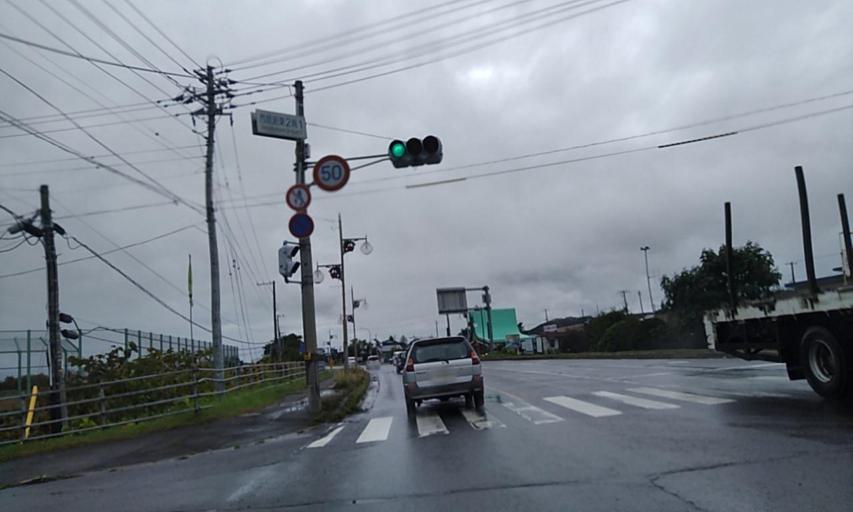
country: JP
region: Hokkaido
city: Kushiro
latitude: 42.9795
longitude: 144.1347
